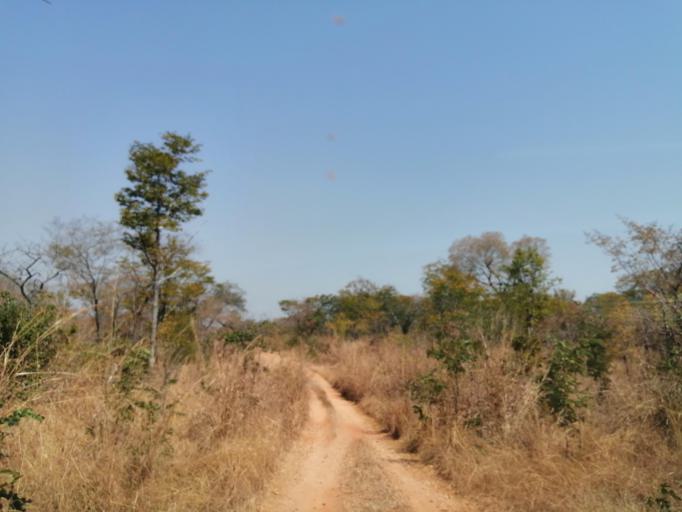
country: ZM
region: Eastern
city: Nyimba
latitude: -14.2586
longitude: 30.0776
